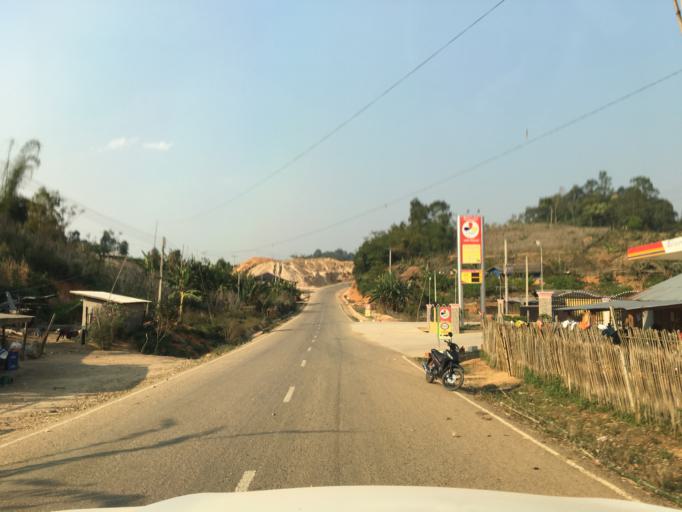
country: LA
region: Houaphan
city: Xam Nua
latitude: 20.5825
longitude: 104.0558
